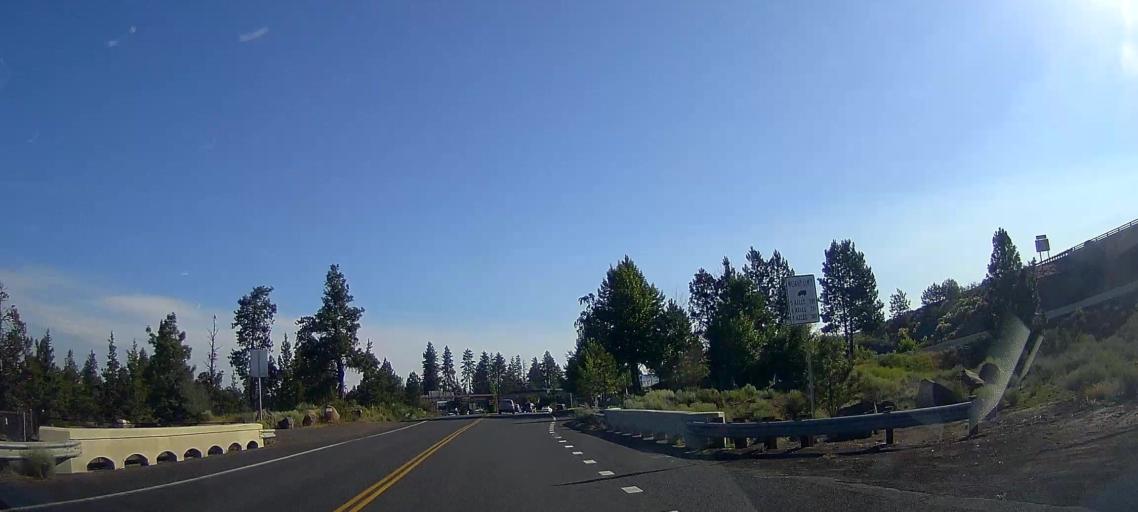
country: US
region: Oregon
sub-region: Deschutes County
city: Bend
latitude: 44.0767
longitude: -121.3052
